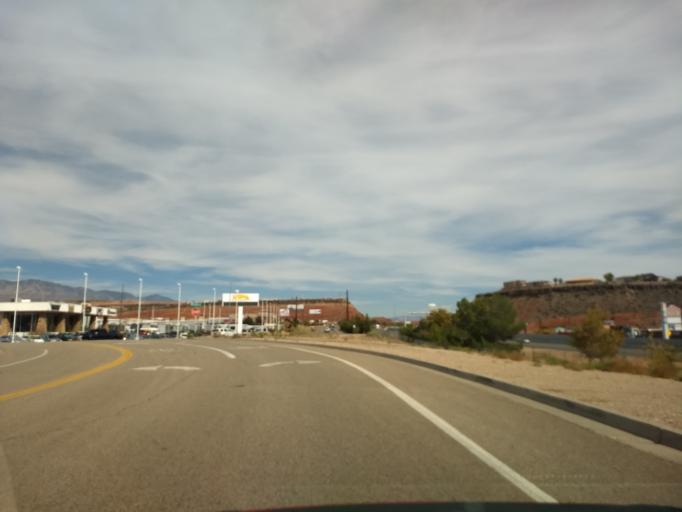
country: US
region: Utah
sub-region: Washington County
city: Saint George
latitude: 37.1123
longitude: -113.5579
